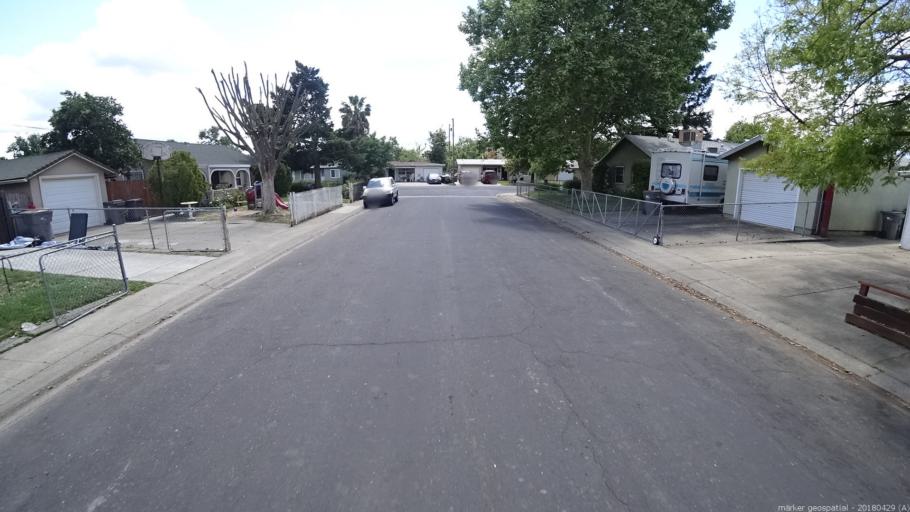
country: US
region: California
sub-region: Yolo County
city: West Sacramento
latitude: 38.5911
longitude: -121.5230
